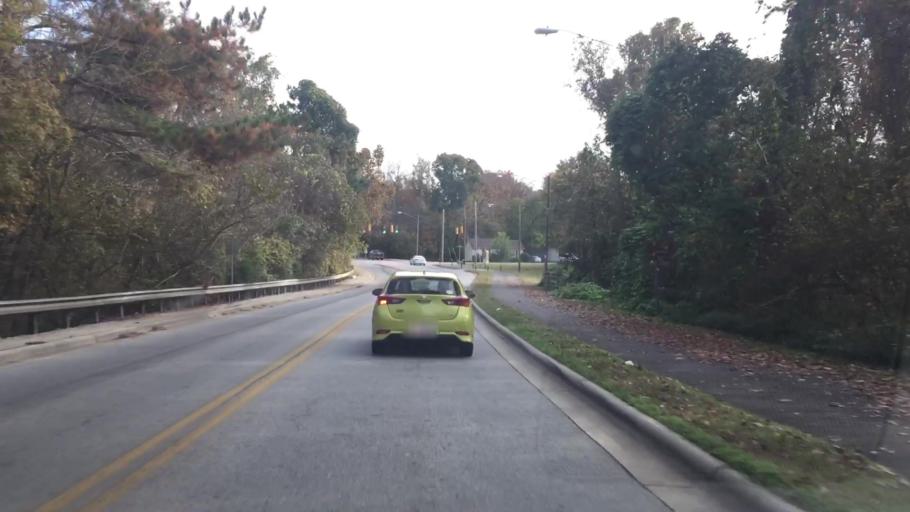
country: US
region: North Carolina
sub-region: Rowan County
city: Salisbury
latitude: 35.6752
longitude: -80.4916
